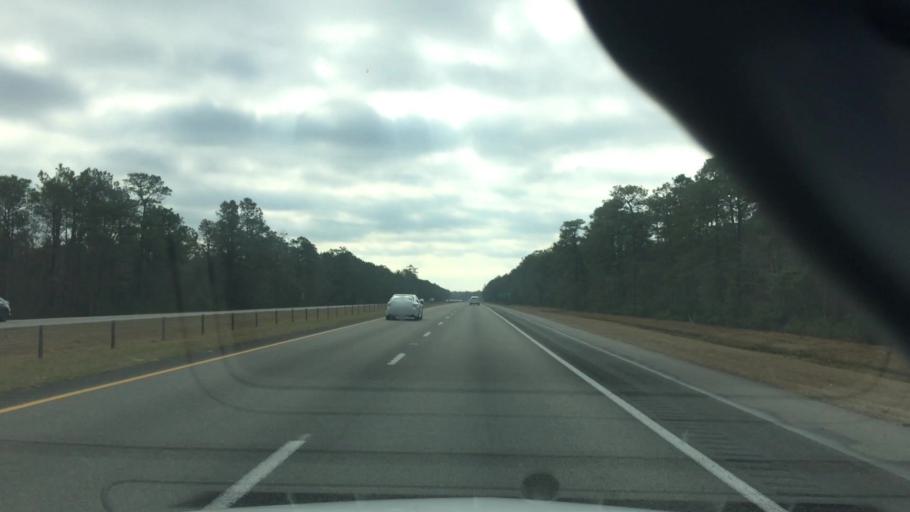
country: US
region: North Carolina
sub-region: New Hanover County
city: Castle Hayne
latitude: 34.3865
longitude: -77.8778
